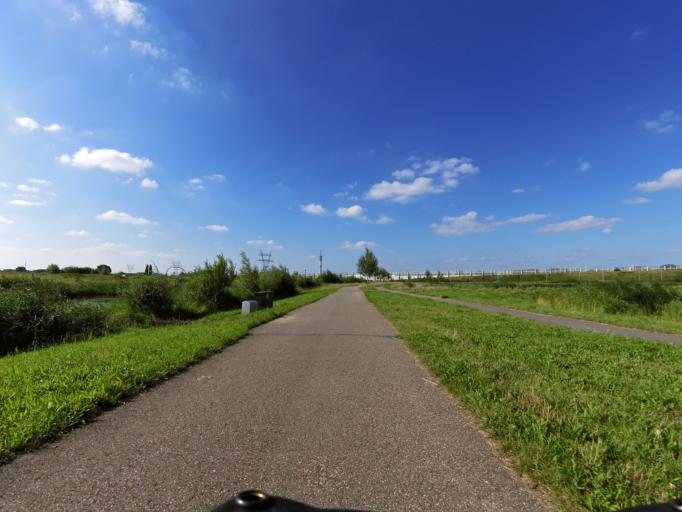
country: NL
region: South Holland
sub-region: Gemeente Binnenmaas
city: Heinenoord
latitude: 51.8585
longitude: 4.4615
